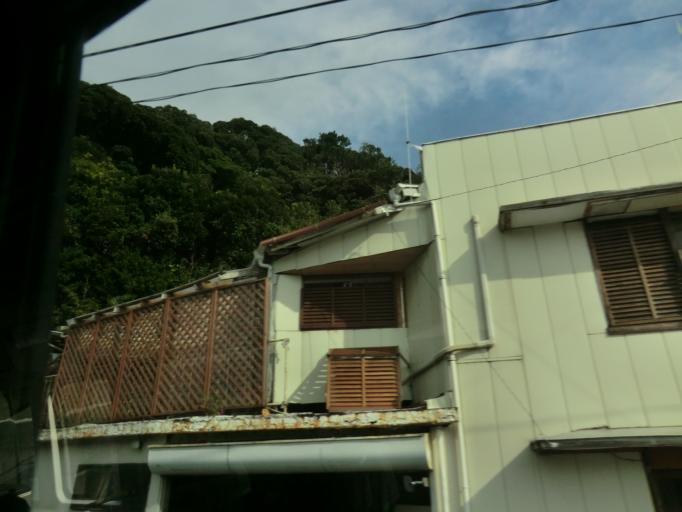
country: JP
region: Chiba
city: Tateyama
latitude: 35.0488
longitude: 139.8346
